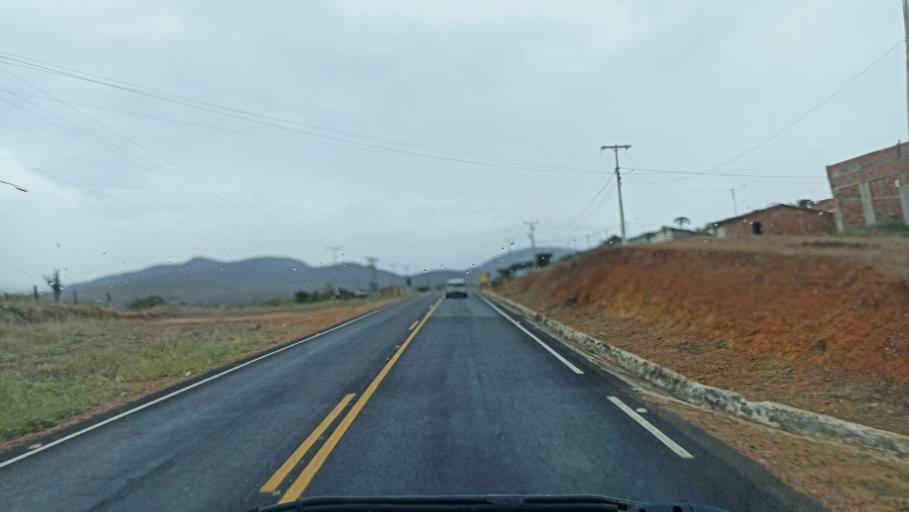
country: BR
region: Bahia
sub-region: Maracas
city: Maracas
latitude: -13.0480
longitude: -40.7429
